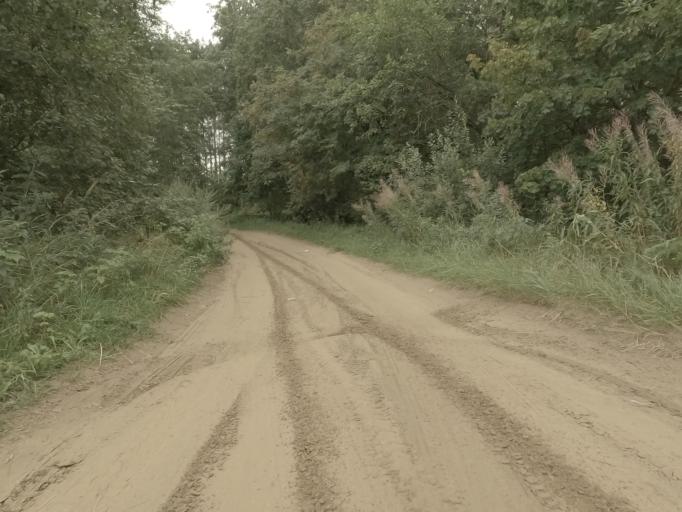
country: RU
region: Leningrad
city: Kirovsk
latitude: 59.8980
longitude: 31.0060
